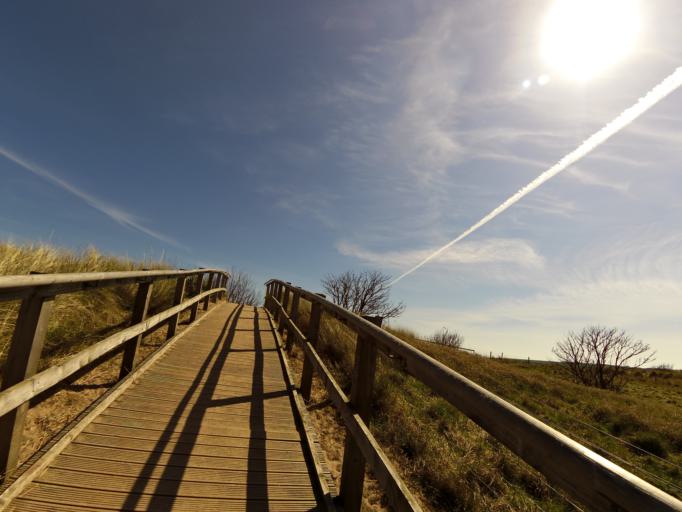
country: GB
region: Scotland
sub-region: Angus
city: Montrose
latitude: 56.6547
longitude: -2.5052
